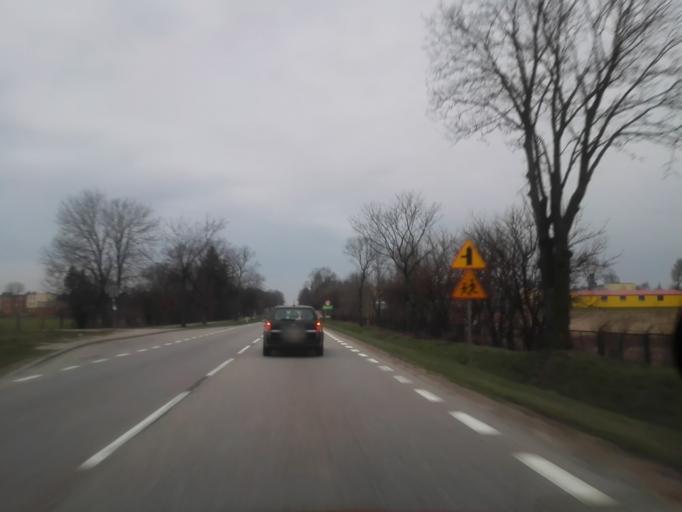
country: PL
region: Podlasie
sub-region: Powiat lomzynski
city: Piatnica
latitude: 53.2137
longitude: 22.1053
